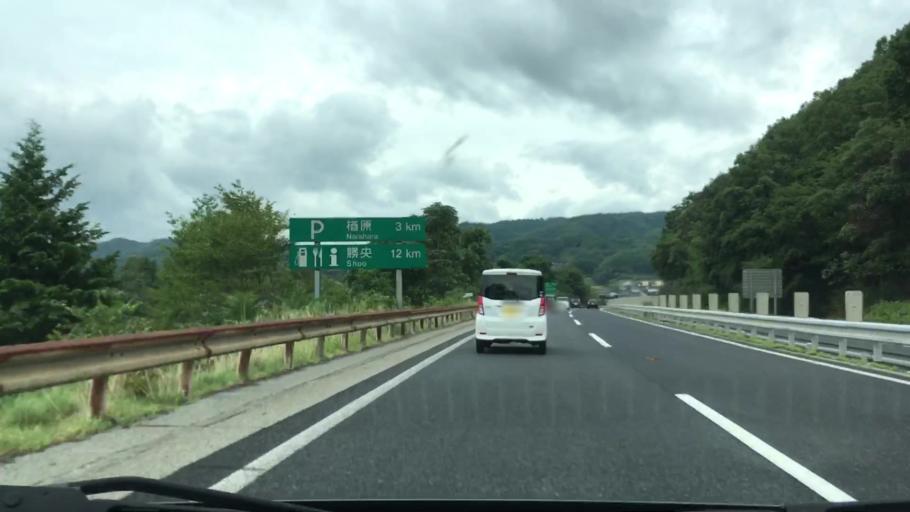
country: JP
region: Okayama
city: Tsuyama
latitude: 35.0158
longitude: 134.2325
